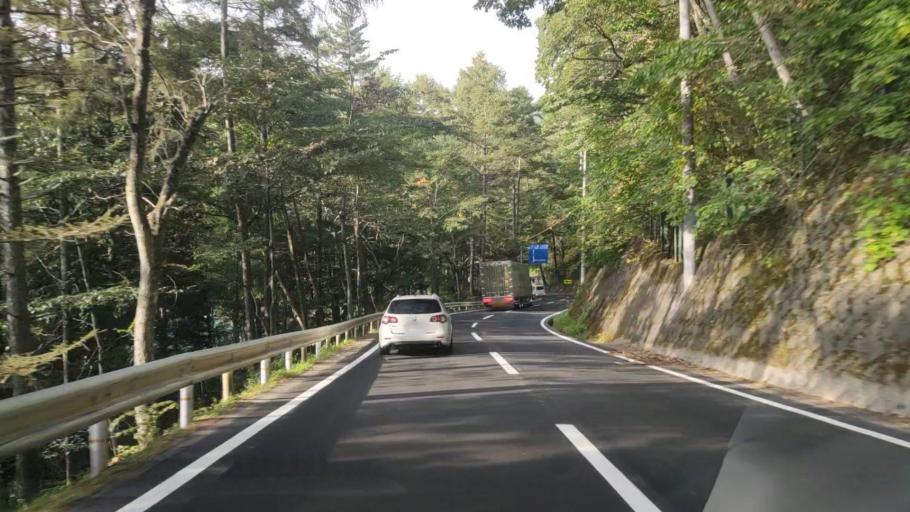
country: JP
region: Nagano
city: Ueda
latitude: 36.4953
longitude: 138.3891
